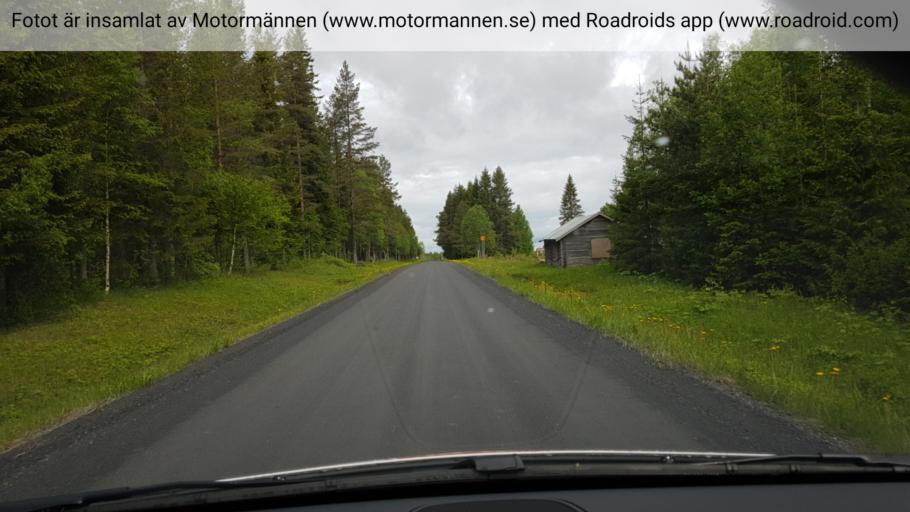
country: SE
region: Jaemtland
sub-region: OEstersunds Kommun
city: Lit
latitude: 63.2252
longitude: 15.0680
